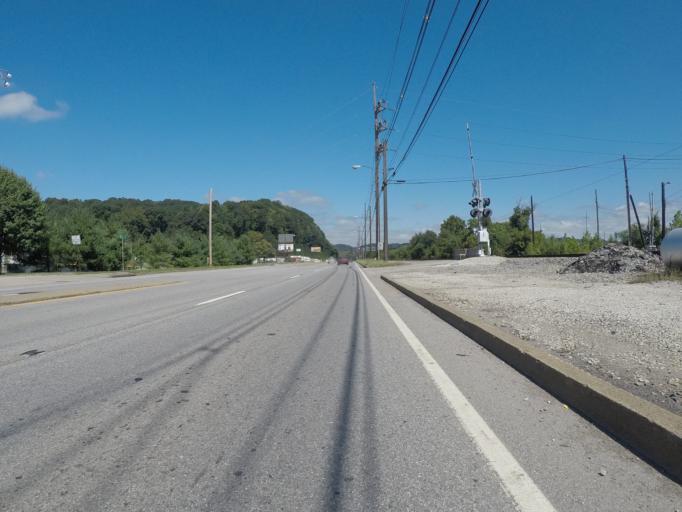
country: US
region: Kentucky
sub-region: Boyd County
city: Ashland
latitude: 38.4538
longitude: -82.6125
